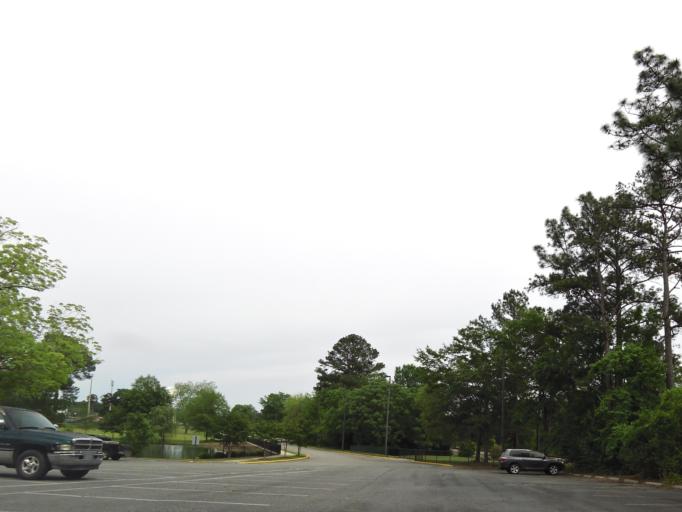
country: US
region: Georgia
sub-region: Bleckley County
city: Cochran
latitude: 32.3787
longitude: -83.3451
